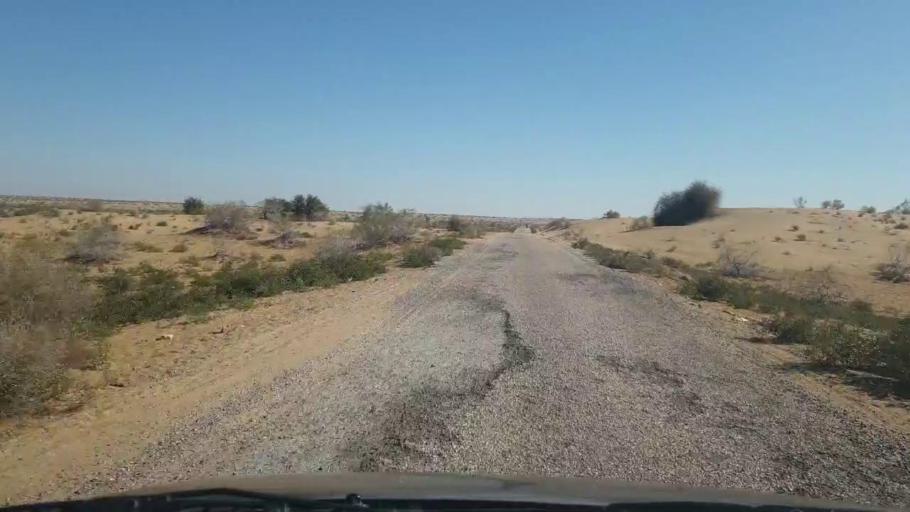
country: PK
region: Sindh
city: Bozdar
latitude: 27.0133
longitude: 68.7883
